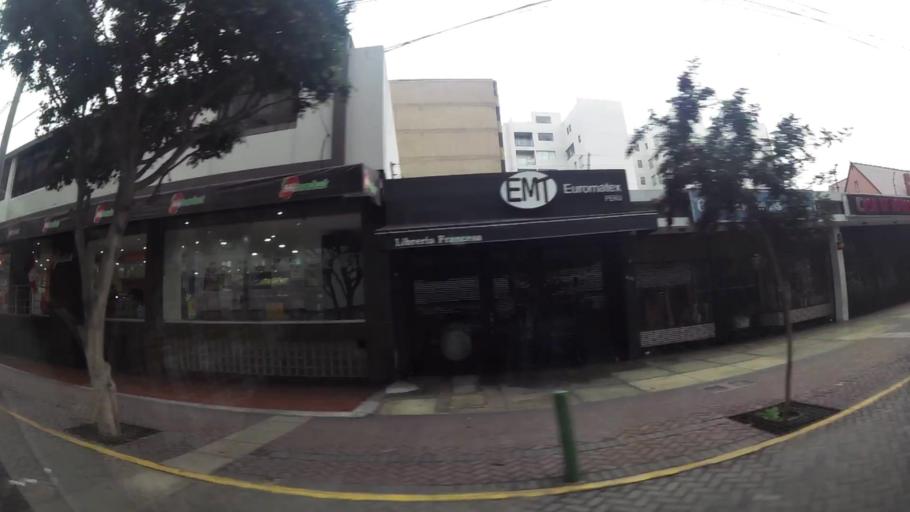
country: PE
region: Lima
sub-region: Lima
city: San Isidro
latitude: -12.1233
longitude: -77.0274
